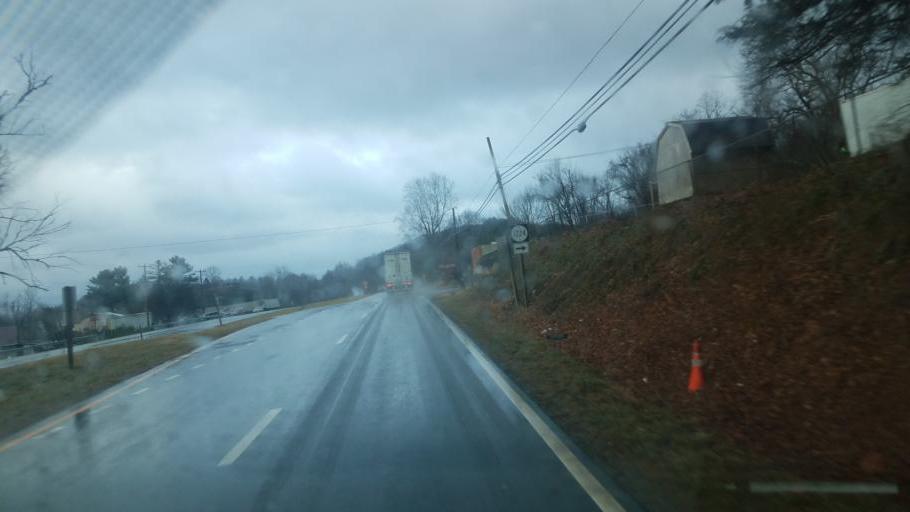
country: US
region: Virginia
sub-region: Giles County
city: Pearisburg
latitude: 37.3086
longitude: -80.7356
